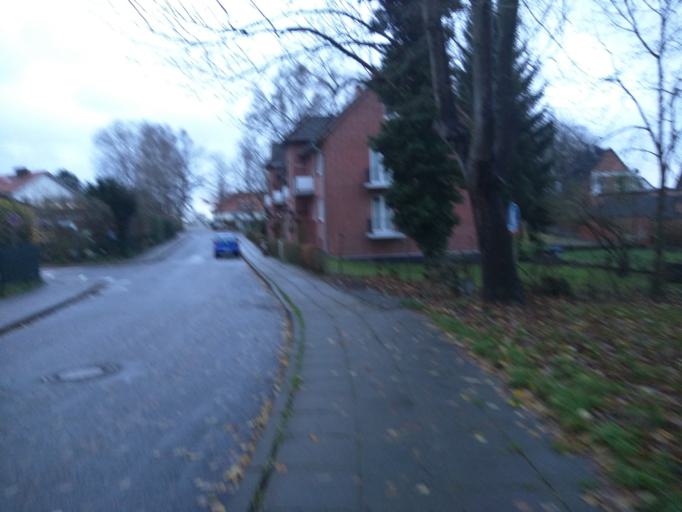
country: DE
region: Schleswig-Holstein
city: Lauenburg
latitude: 53.3728
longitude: 10.5459
